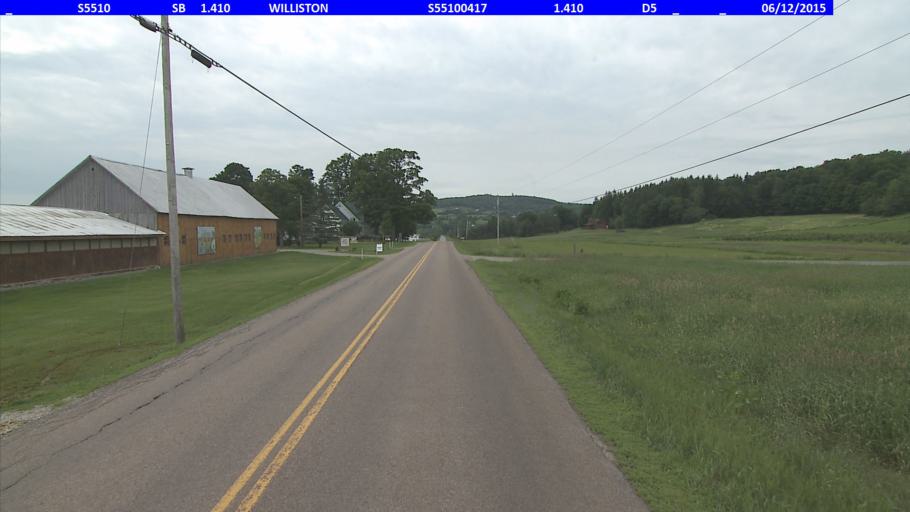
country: US
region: Vermont
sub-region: Chittenden County
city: Williston
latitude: 44.3925
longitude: -73.0945
